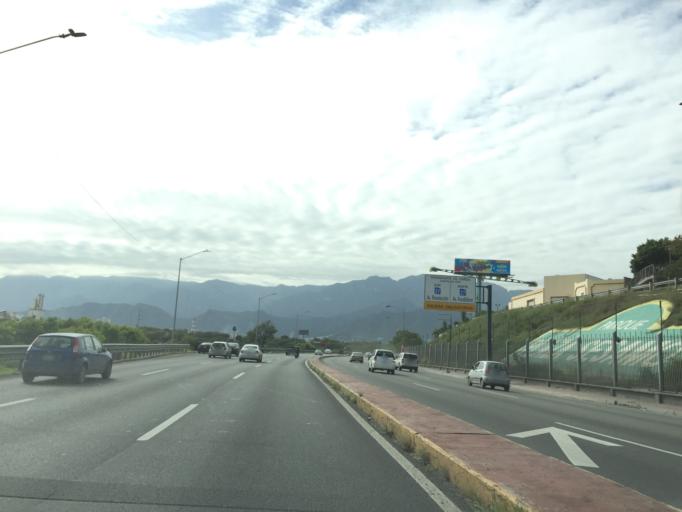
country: MX
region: Nuevo Leon
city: Guadalupe
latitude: 25.6785
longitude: -100.2755
